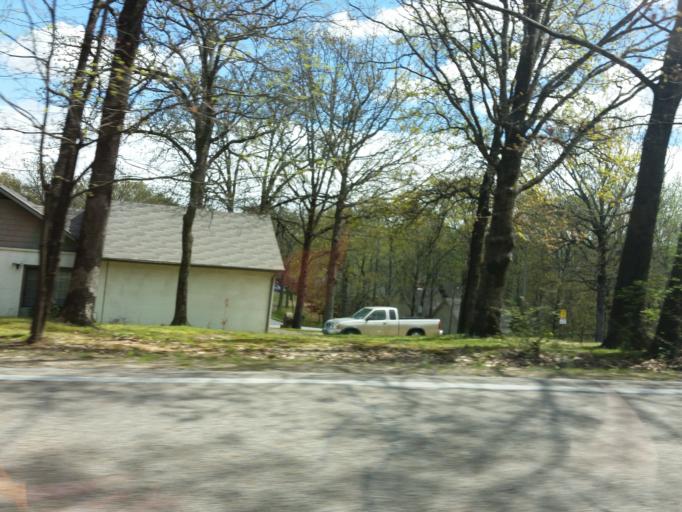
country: US
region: Arkansas
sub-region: Craighead County
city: Jonesboro
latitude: 35.8162
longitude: -90.7016
